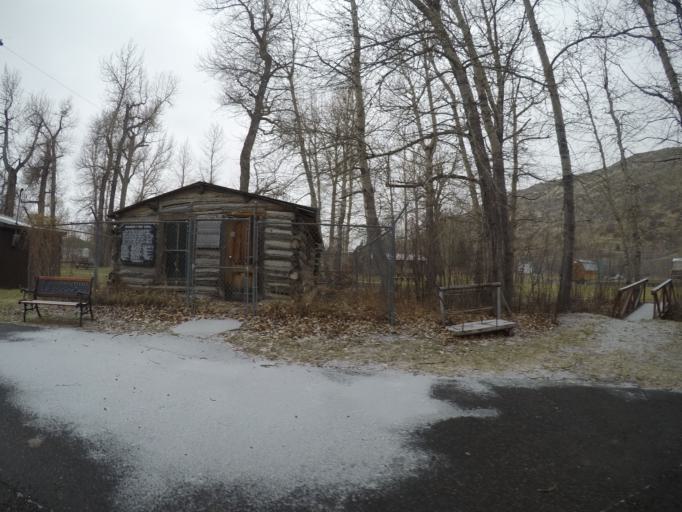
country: US
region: Montana
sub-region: Stillwater County
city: Absarokee
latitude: 45.5180
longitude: -109.4495
